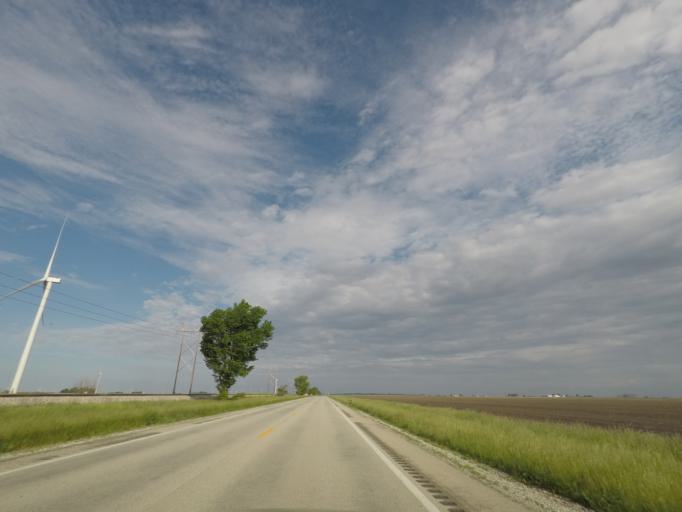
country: US
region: Illinois
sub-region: Logan County
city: Mount Pulaski
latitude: 39.9872
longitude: -89.2295
